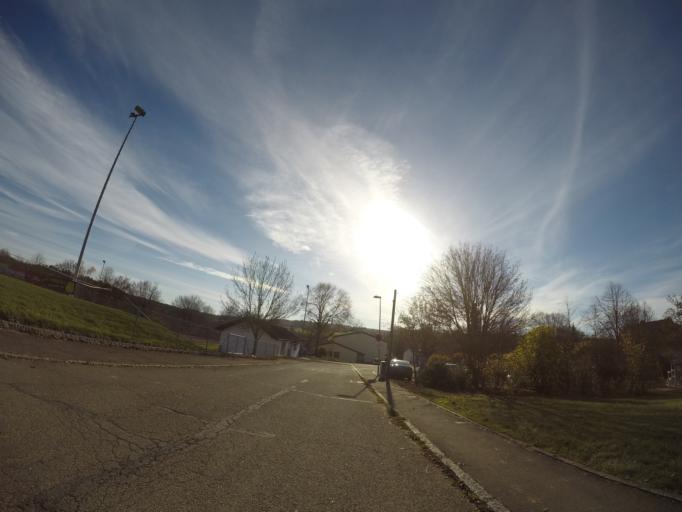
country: DE
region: Baden-Wuerttemberg
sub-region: Tuebingen Region
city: Dornstadt
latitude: 48.4381
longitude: 9.9435
